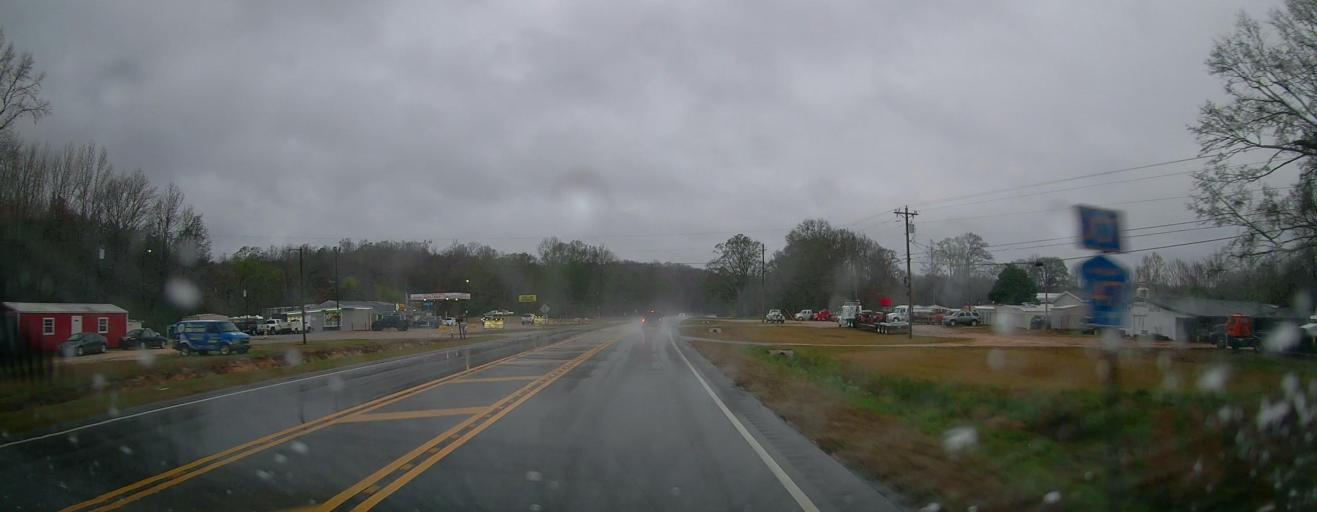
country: US
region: Alabama
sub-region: Autauga County
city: Prattville
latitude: 32.4737
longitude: -86.5192
